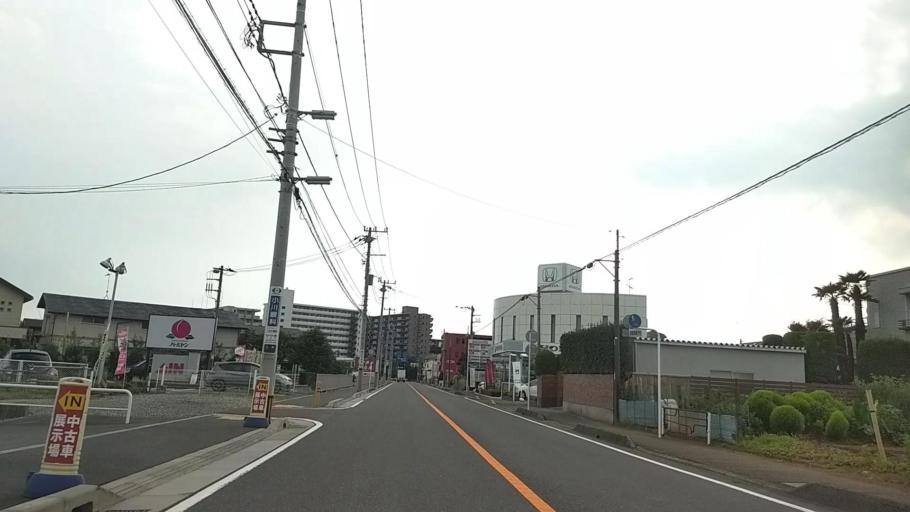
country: JP
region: Kanagawa
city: Atsugi
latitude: 35.4529
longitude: 139.3818
